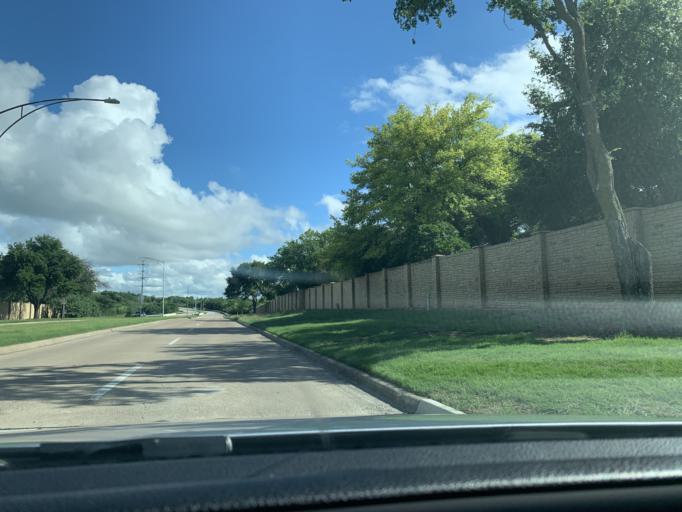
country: US
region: Texas
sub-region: Dallas County
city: Grand Prairie
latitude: 32.6615
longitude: -97.0421
